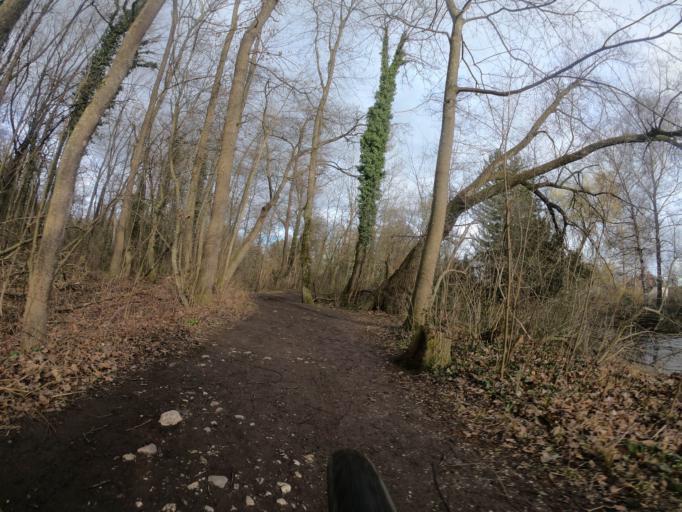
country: DE
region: Bavaria
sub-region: Upper Bavaria
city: Fuerstenfeldbruck
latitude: 48.1793
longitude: 11.2692
